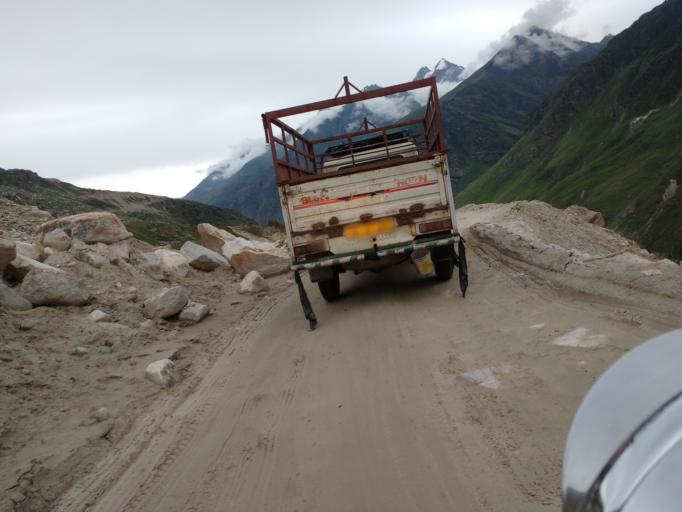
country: IN
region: Himachal Pradesh
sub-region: Kulu
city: Manali
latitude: 32.3786
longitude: 77.2681
